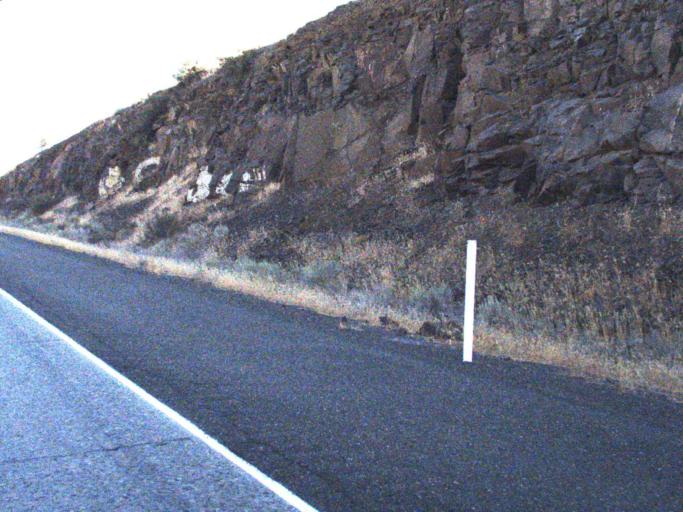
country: US
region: Washington
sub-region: Kittitas County
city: Kittitas
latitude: 46.8157
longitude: -120.3544
